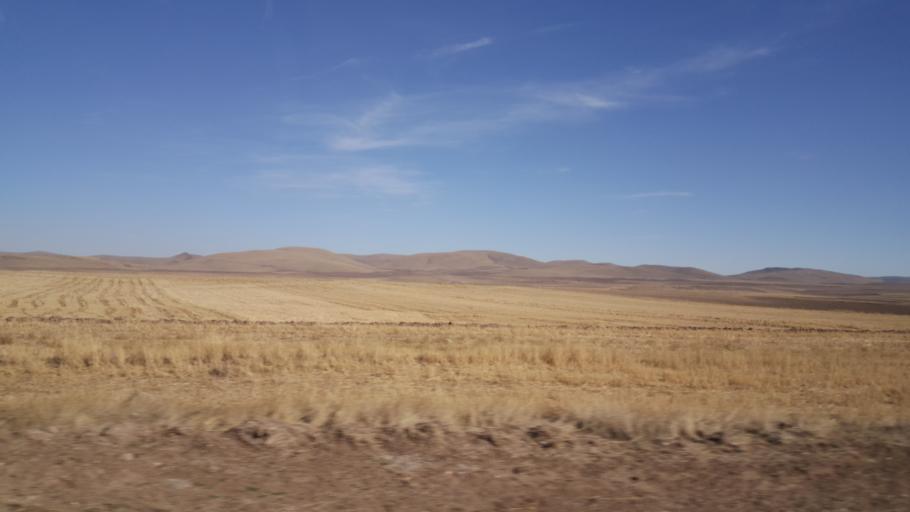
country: TR
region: Ankara
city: Yenice
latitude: 39.2920
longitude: 32.7577
